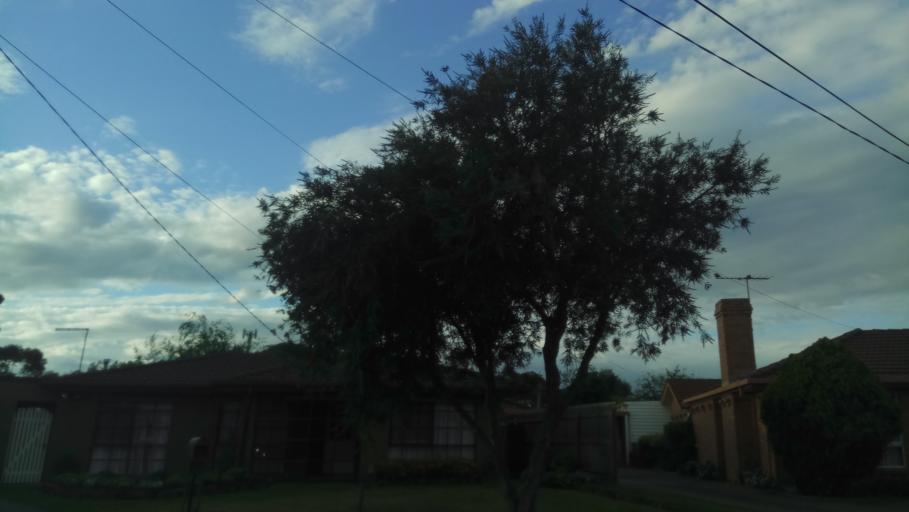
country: AU
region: Victoria
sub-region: Hobsons Bay
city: Altona Meadows
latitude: -37.8721
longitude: 144.7880
